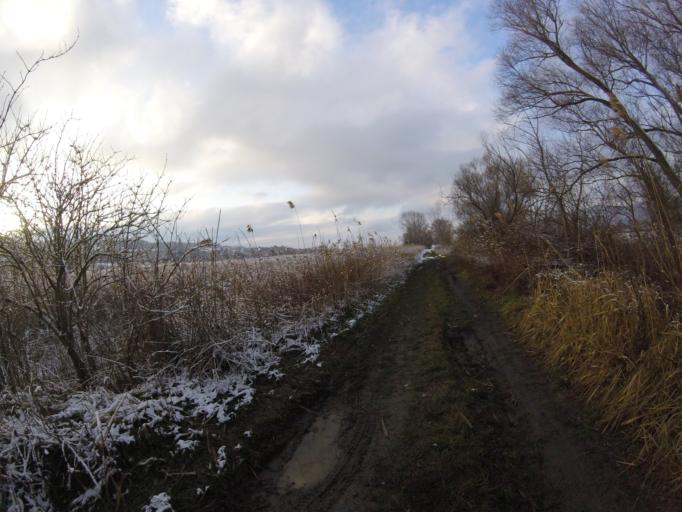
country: HU
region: Komarom-Esztergom
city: Esztergom
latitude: 47.8009
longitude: 18.7880
